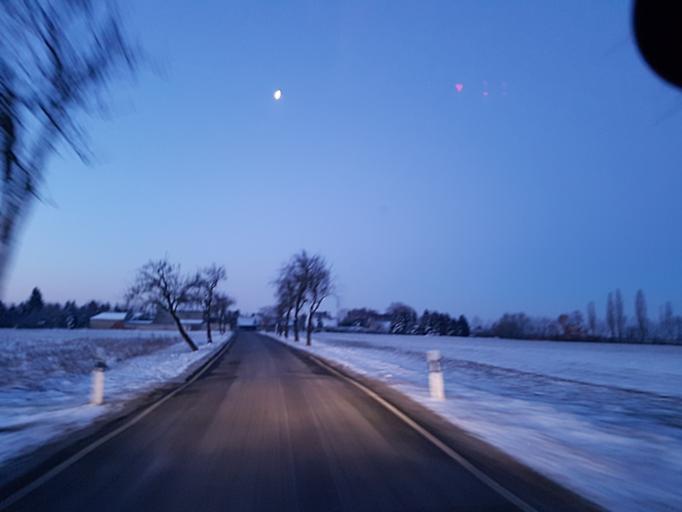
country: DE
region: Brandenburg
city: Falkenberg
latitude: 51.5061
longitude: 13.2903
